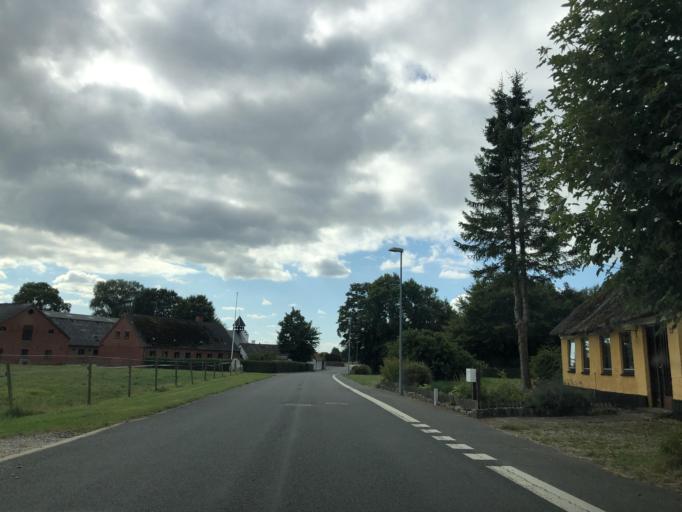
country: DK
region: Central Jutland
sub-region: Viborg Kommune
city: Viborg
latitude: 56.5800
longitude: 9.3843
